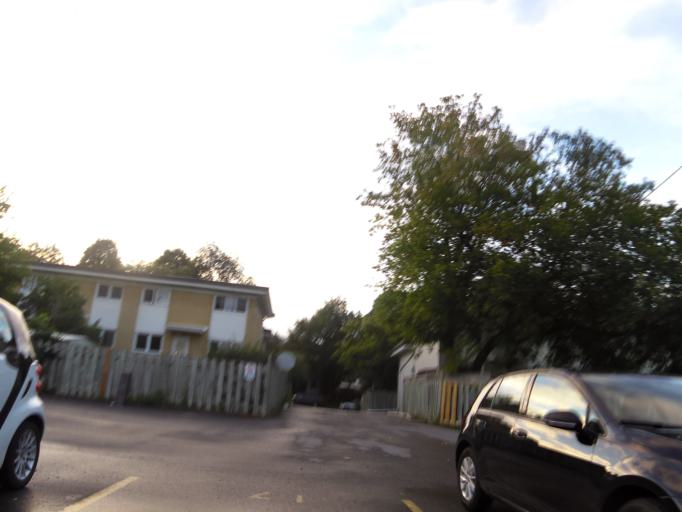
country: CA
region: Ontario
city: Bells Corners
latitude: 45.3543
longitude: -75.7864
